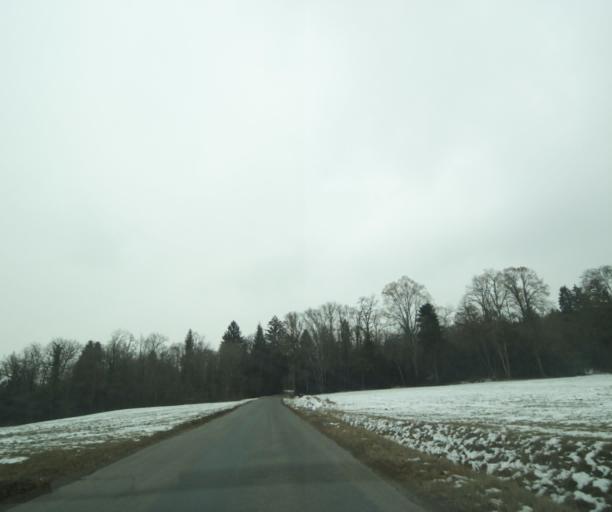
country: FR
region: Rhone-Alpes
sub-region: Departement de la Haute-Savoie
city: Cornier
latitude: 46.1186
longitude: 6.2909
